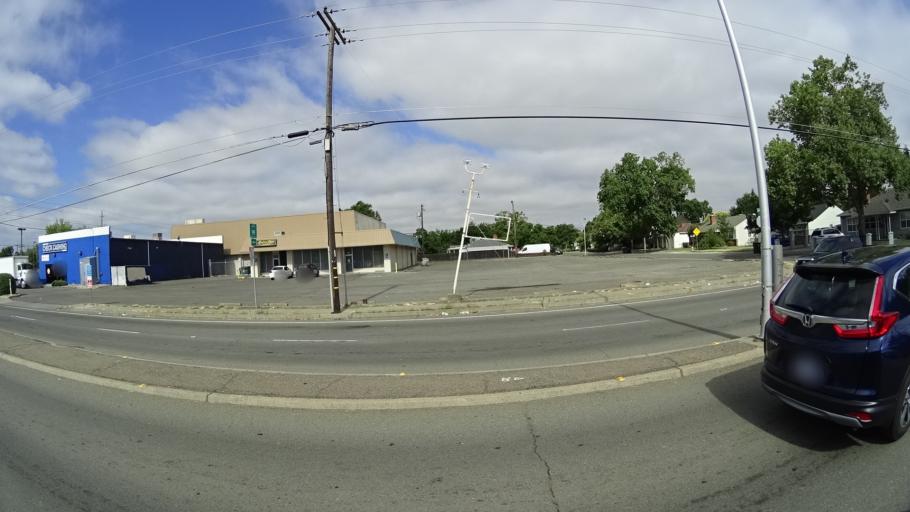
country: US
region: California
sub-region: Sacramento County
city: Parkway
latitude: 38.5256
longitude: -121.4831
